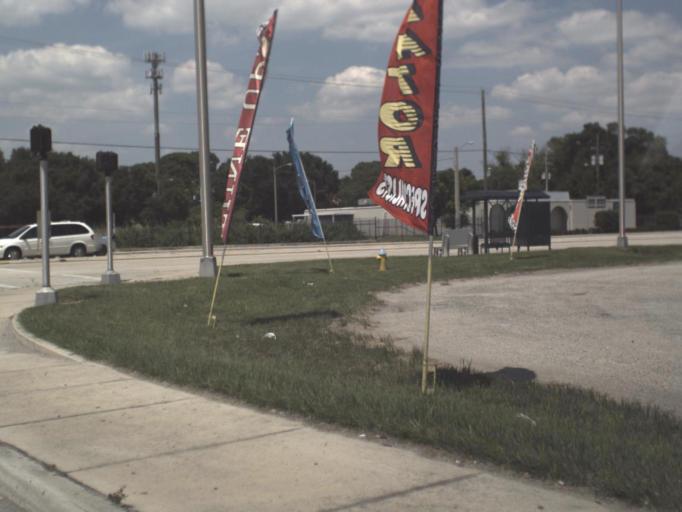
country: US
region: Florida
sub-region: Hillsborough County
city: Palm River-Clair Mel
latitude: 27.9226
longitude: -82.4018
